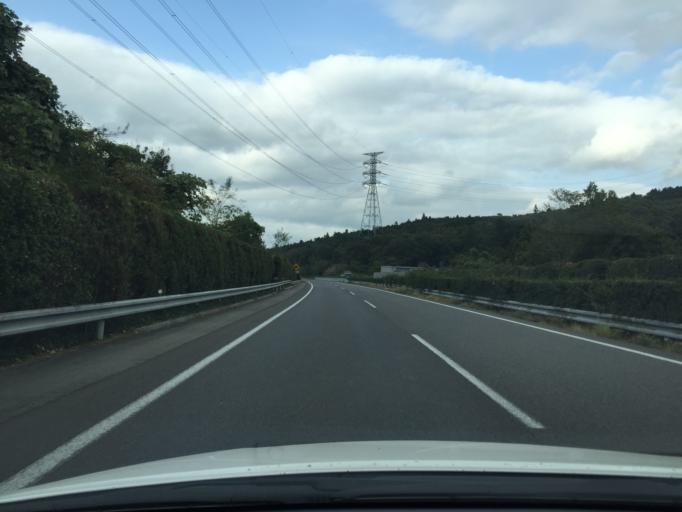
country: JP
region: Ibaraki
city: Kitaibaraki
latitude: 36.9354
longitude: 140.7703
